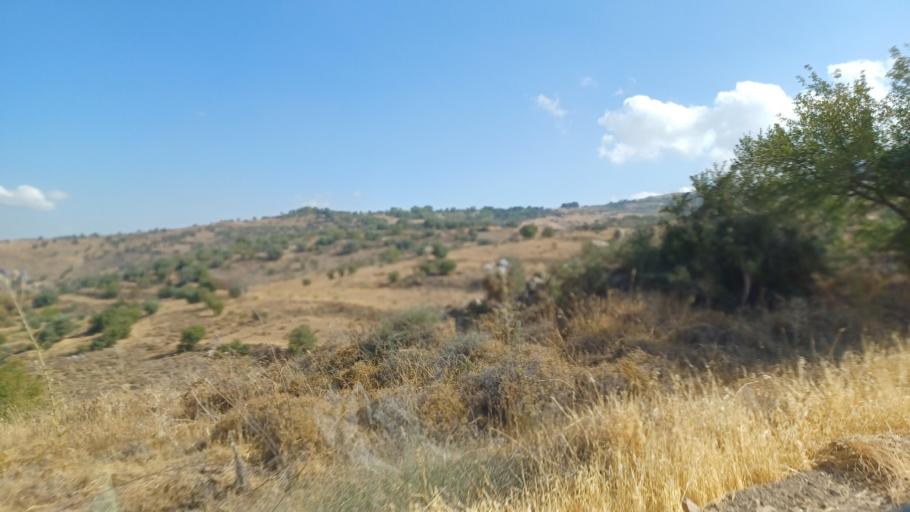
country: CY
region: Pafos
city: Mesogi
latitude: 34.8758
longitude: 32.5976
